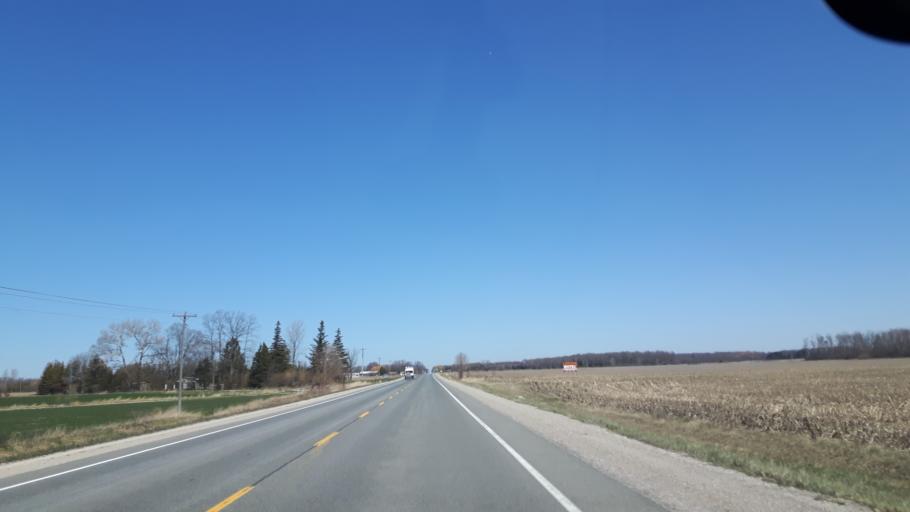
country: CA
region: Ontario
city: Goderich
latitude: 43.6334
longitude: -81.7057
